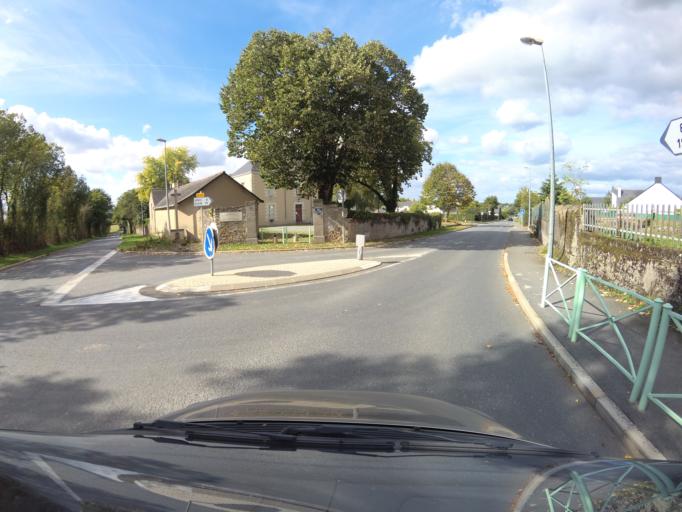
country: FR
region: Pays de la Loire
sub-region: Departement de la Loire-Atlantique
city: Casson
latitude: 47.3866
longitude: -1.5618
